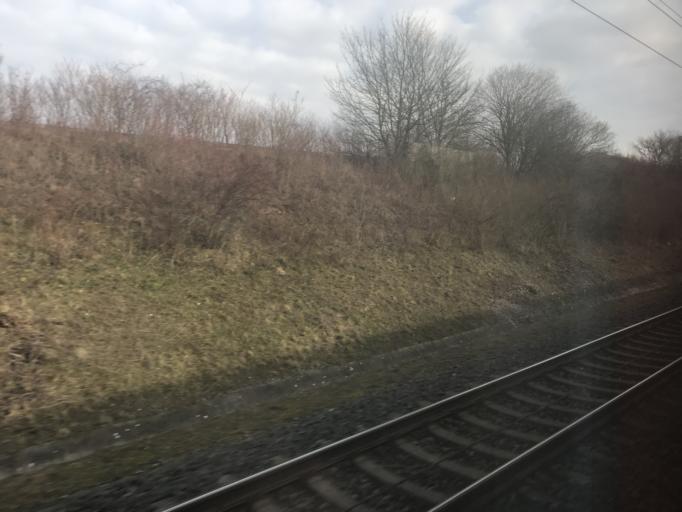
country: DE
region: Baden-Wuerttemberg
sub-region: Regierungsbezirk Stuttgart
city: Markgroningen
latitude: 48.8910
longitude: 9.0786
